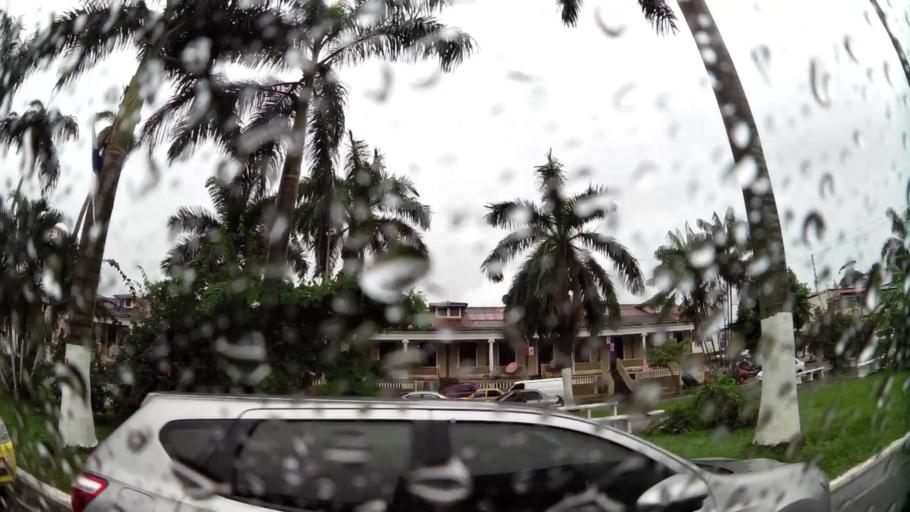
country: PA
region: Colon
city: Colon
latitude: 9.3632
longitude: -79.9032
